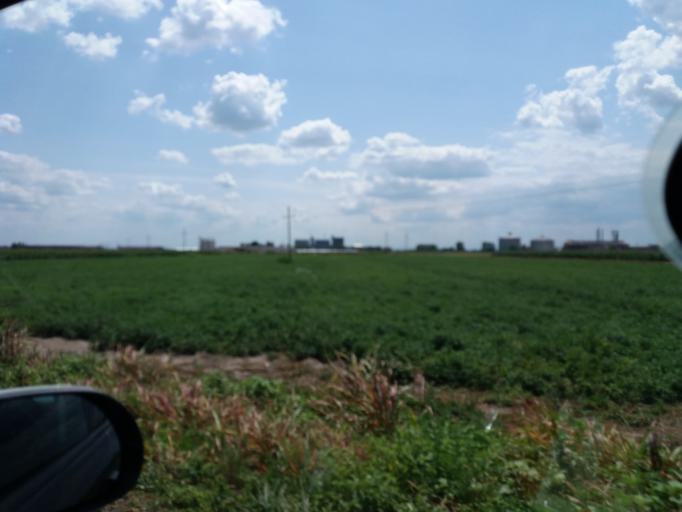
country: RS
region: Autonomna Pokrajina Vojvodina
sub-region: Sremski Okrug
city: Pecinci
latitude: 44.8984
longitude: 19.9610
